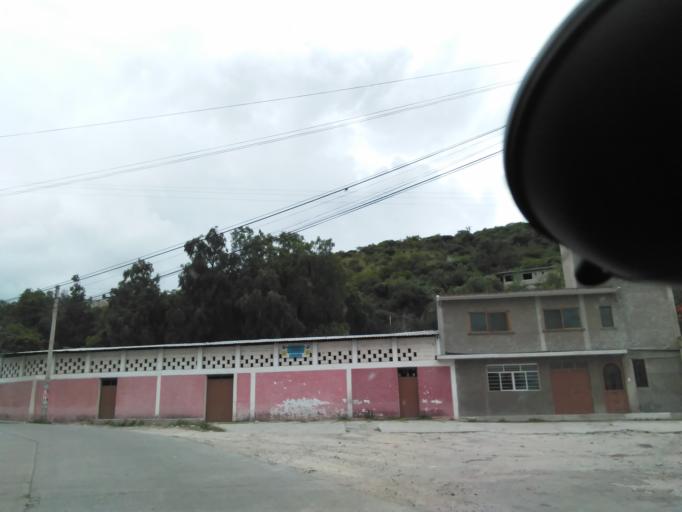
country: MX
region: Hidalgo
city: Tula de Allende
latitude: 20.0602
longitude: -99.3487
